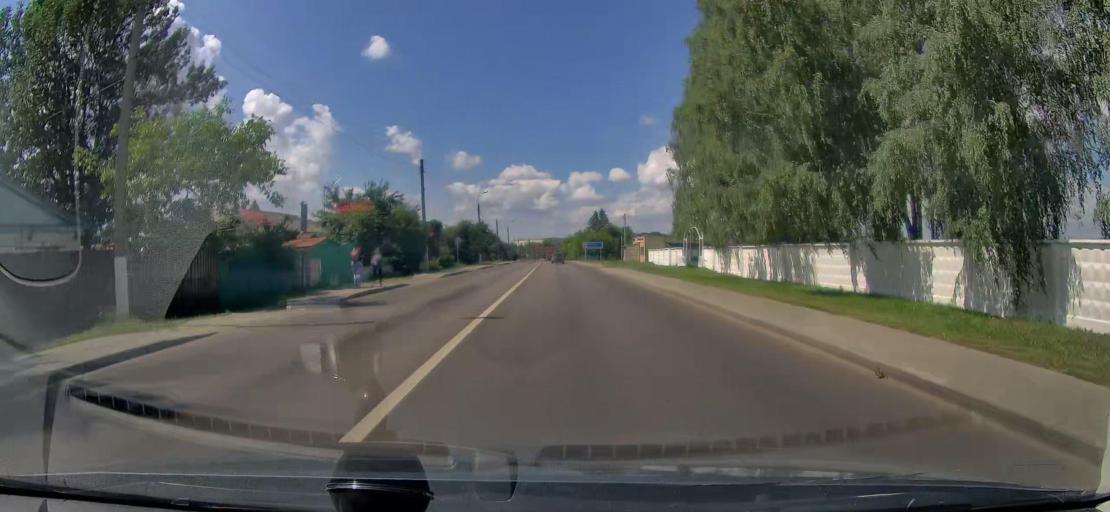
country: RU
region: Kursk
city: Zolotukhino
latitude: 51.9714
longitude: 36.3001
